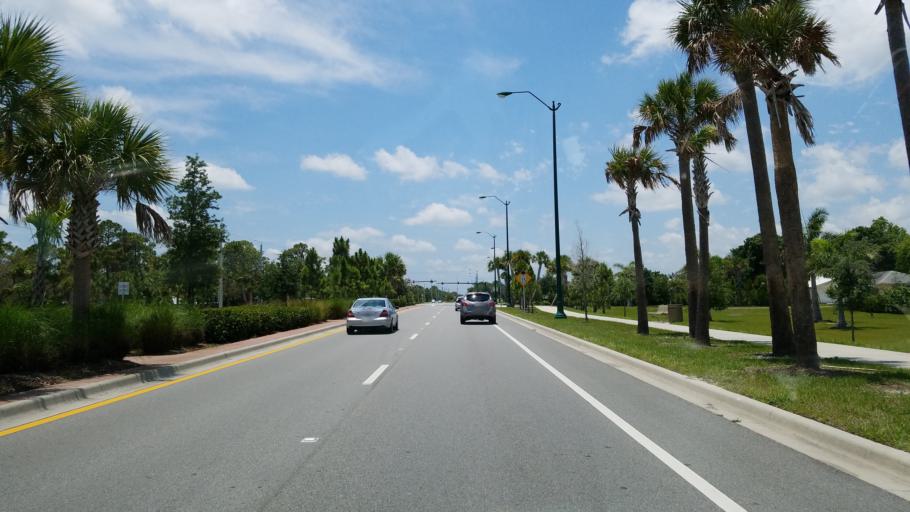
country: US
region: Florida
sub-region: Martin County
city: Palm City
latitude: 27.1612
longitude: -80.2669
